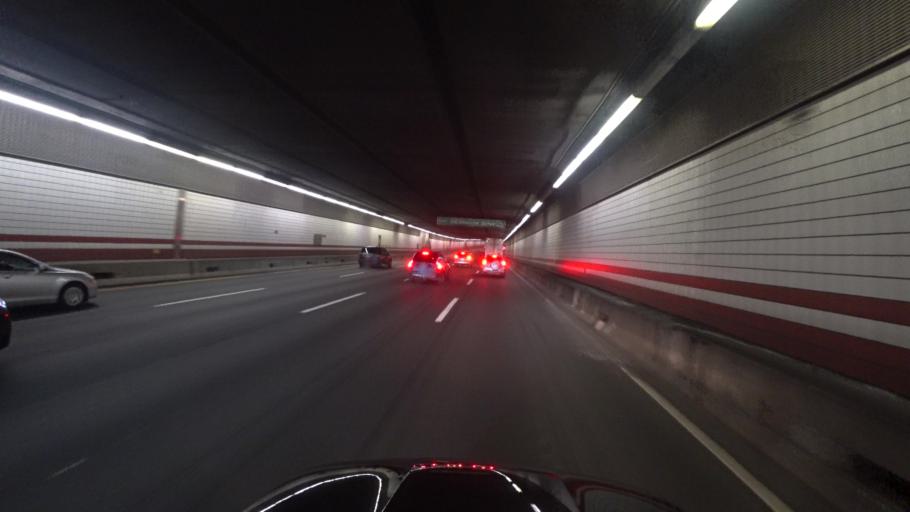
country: US
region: Massachusetts
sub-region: Suffolk County
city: Boston
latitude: 42.3598
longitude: -71.0587
